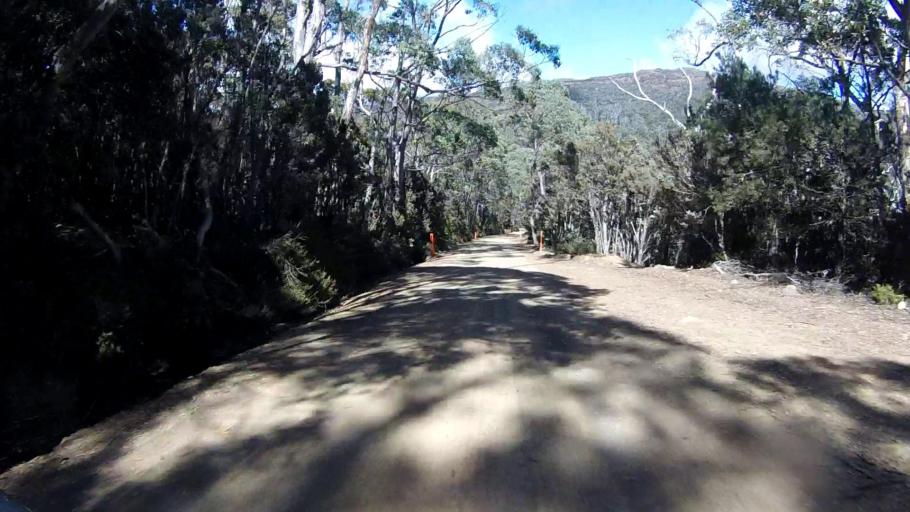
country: AU
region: Tasmania
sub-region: Derwent Valley
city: New Norfolk
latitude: -42.6866
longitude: 146.6038
